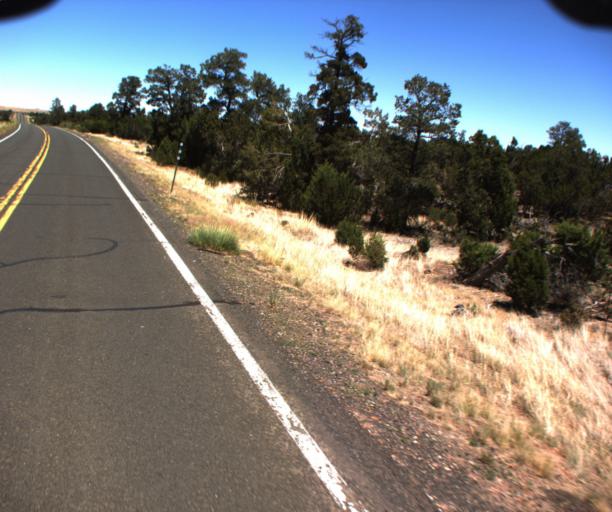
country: US
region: Arizona
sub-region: Coconino County
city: LeChee
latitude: 34.7120
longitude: -111.0939
